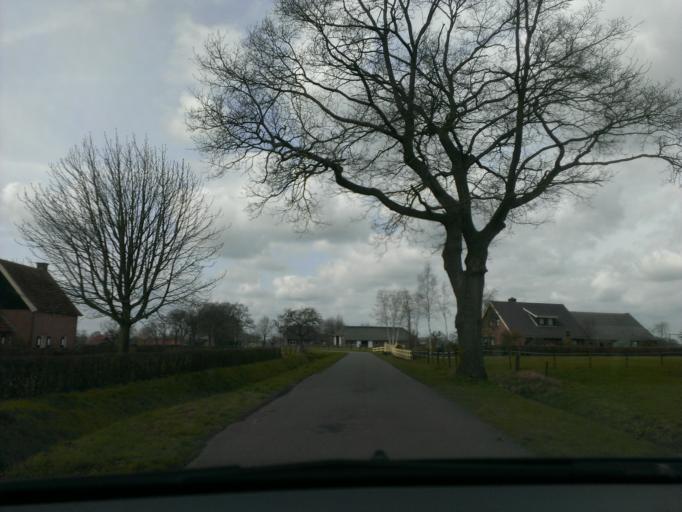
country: NL
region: Overijssel
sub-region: Gemeente Borne
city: Borne
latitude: 52.3076
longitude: 6.7300
